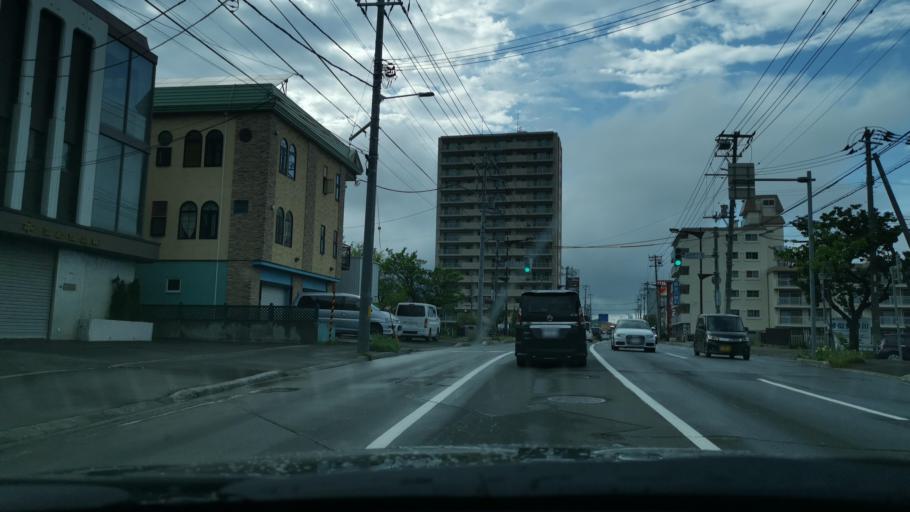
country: JP
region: Hokkaido
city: Sapporo
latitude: 43.0727
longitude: 141.2858
